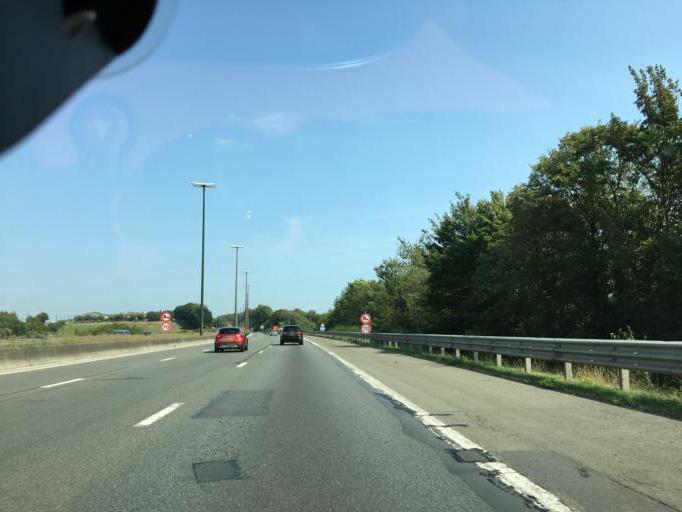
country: BE
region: Wallonia
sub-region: Province du Hainaut
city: Chapelle-lez-Herlaimont
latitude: 50.4783
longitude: 4.2946
